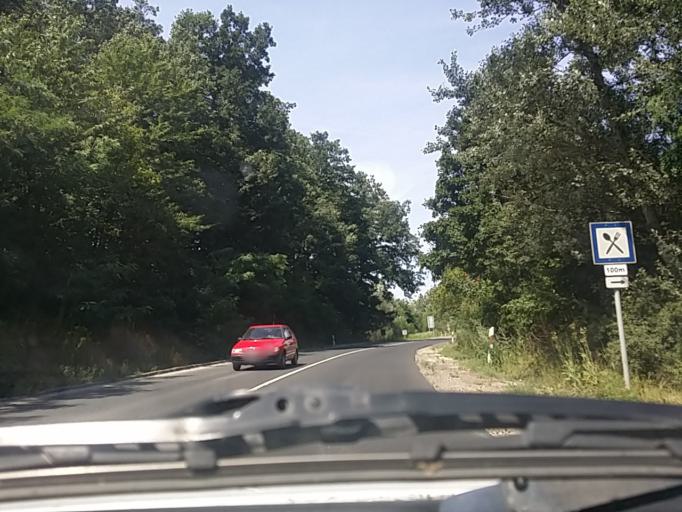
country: HU
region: Pest
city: Pilisszentivan
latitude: 47.6214
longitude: 18.8657
